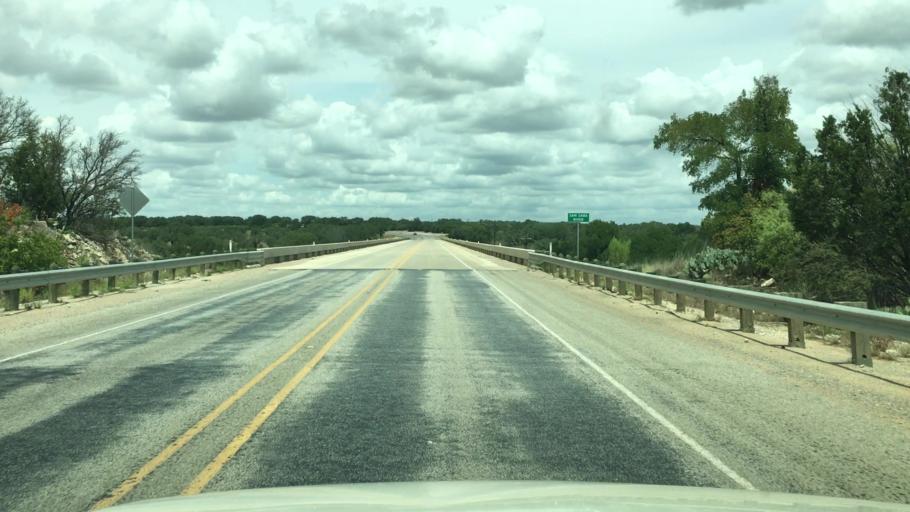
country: US
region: Texas
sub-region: McCulloch County
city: Brady
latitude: 31.0131
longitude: -99.2090
